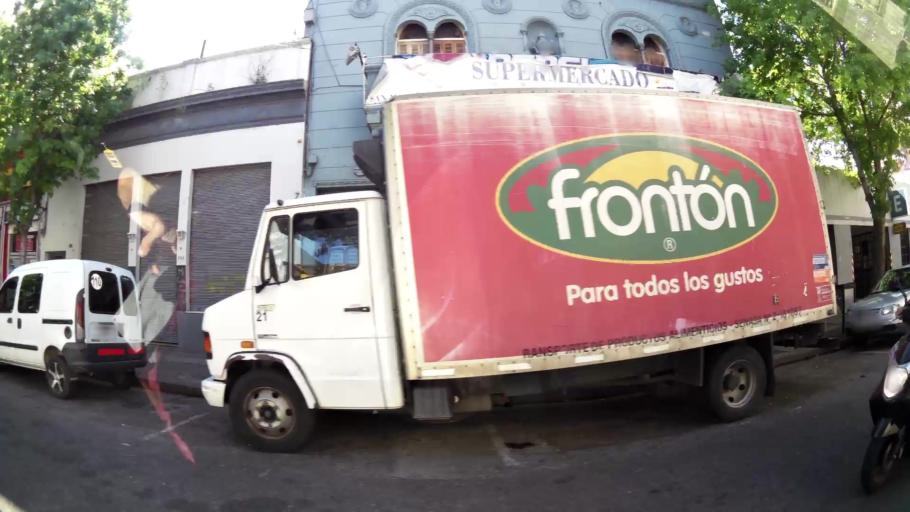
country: AR
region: Santa Fe
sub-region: Departamento de Rosario
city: Rosario
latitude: -32.9559
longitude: -60.6390
